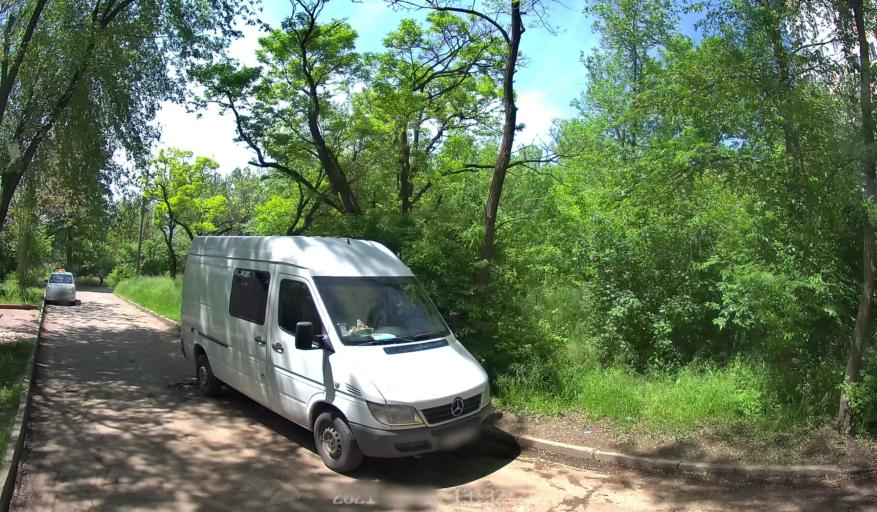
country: MD
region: Chisinau
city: Chisinau
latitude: 47.0558
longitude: 28.8208
